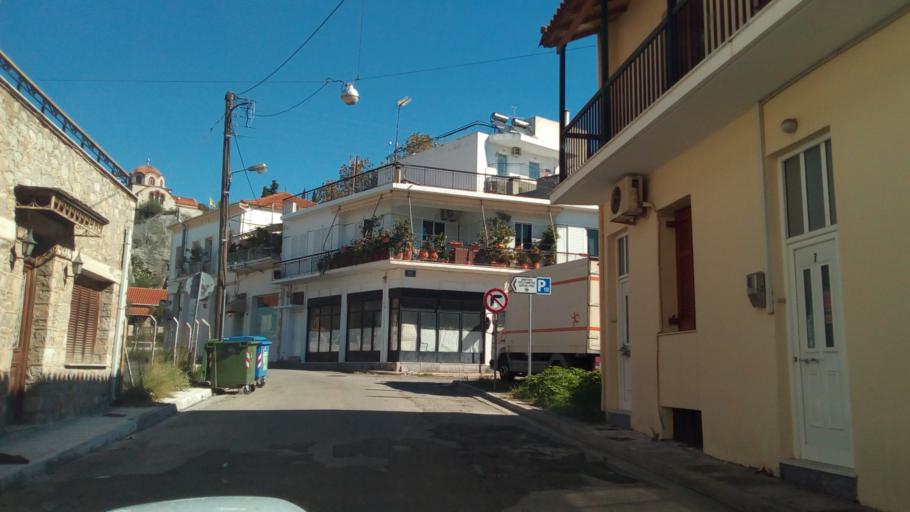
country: GR
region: West Greece
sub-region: Nomos Aitolias kai Akarnanias
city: Nafpaktos
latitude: 38.3936
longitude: 21.8400
